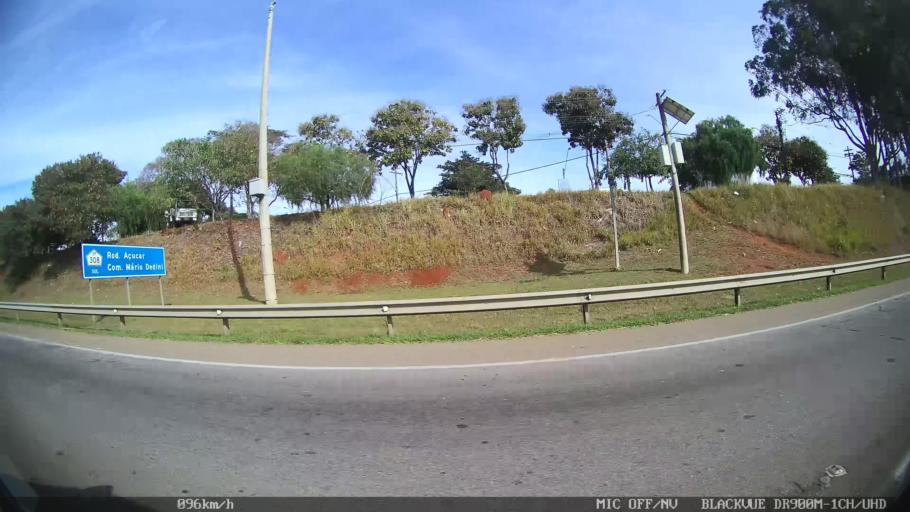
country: BR
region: Sao Paulo
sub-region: Piracicaba
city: Piracicaba
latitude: -22.7687
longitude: -47.5946
